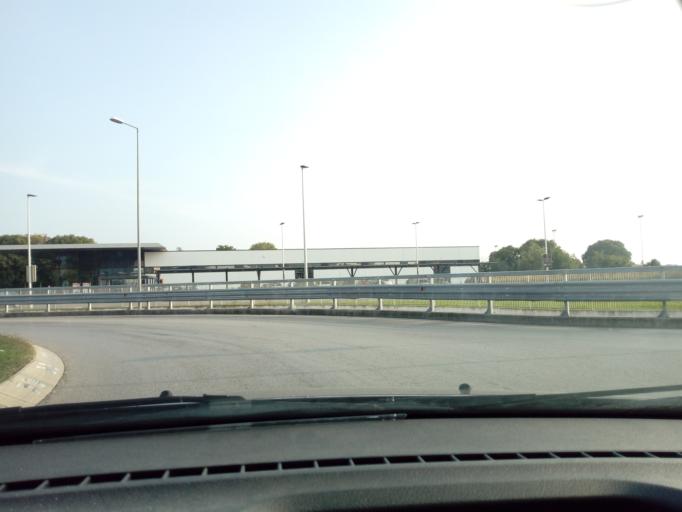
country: IT
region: Friuli Venezia Giulia
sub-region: Provincia di Udine
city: Manzano
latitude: 45.9863
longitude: 13.3723
